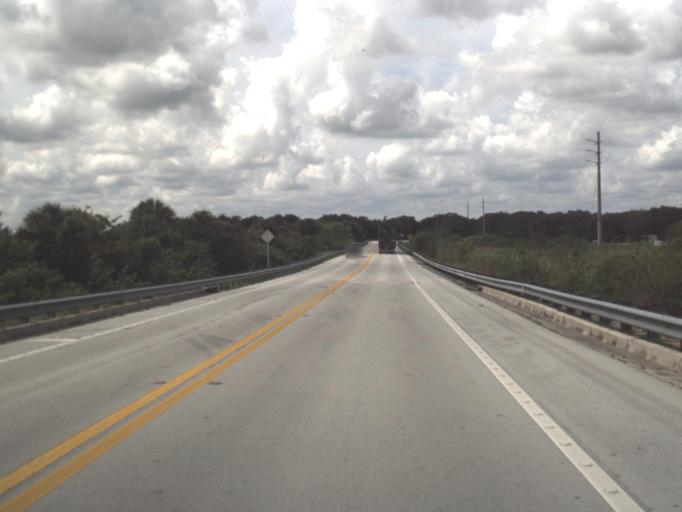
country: US
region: Florida
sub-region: Glades County
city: Buckhead Ridge
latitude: 27.2384
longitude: -80.9837
